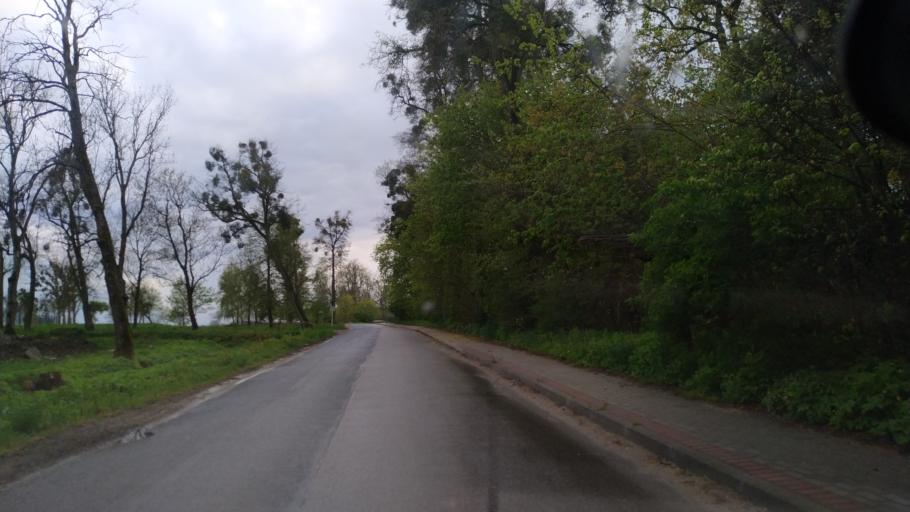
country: PL
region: Pomeranian Voivodeship
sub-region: Powiat starogardzki
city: Smetowo Graniczne
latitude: 53.7349
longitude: 18.6475
